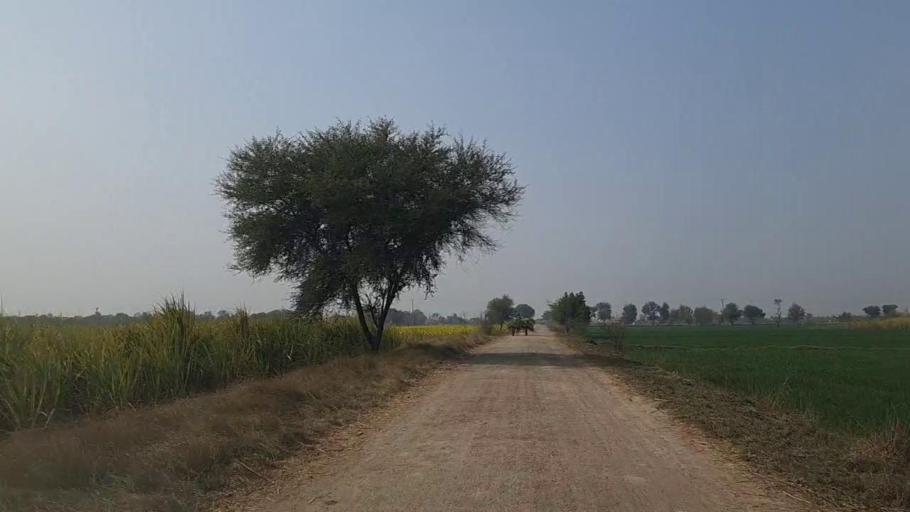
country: PK
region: Sindh
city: Daur
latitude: 26.4325
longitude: 68.4482
